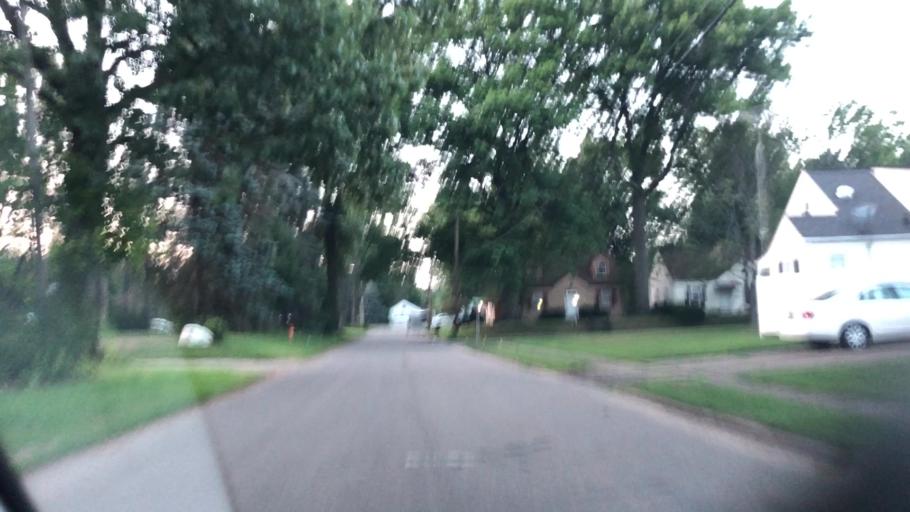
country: US
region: Ohio
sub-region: Stark County
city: Massillon
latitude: 40.8266
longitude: -81.5084
